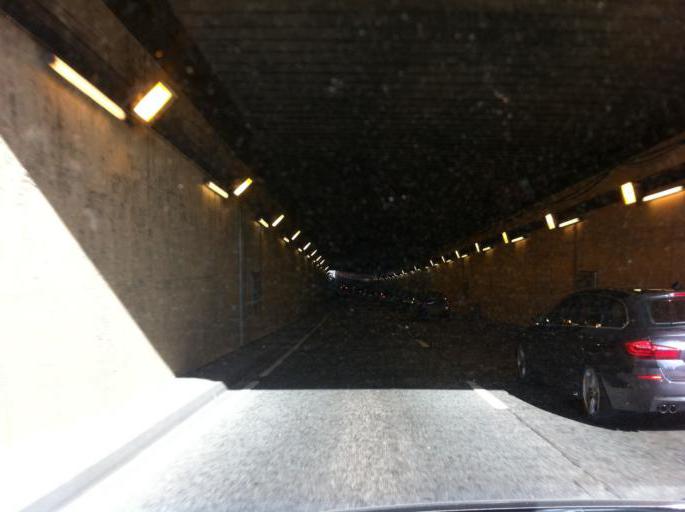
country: GB
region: England
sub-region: Greater London
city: Ealing Broadway
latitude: 51.5294
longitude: -0.2911
